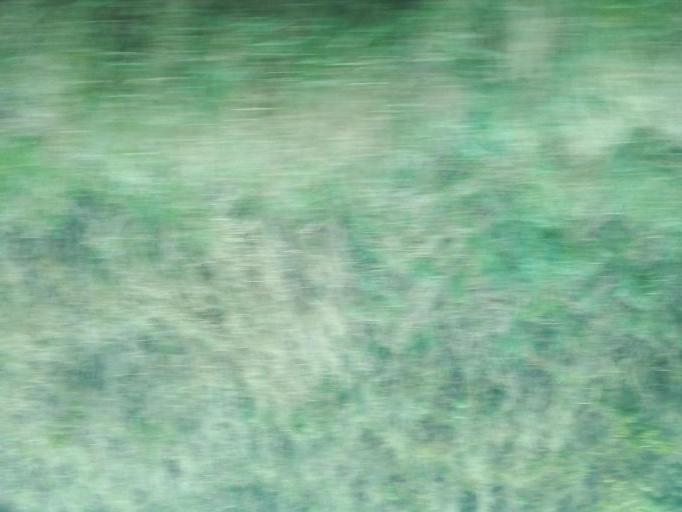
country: BR
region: Minas Gerais
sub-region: Timoteo
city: Timoteo
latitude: -19.5373
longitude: -42.6859
